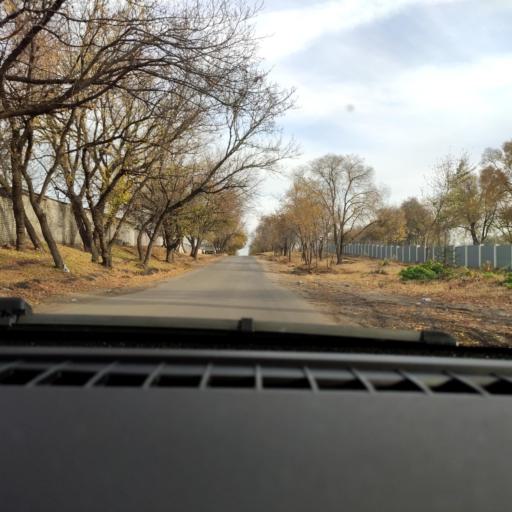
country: RU
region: Voronezj
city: Voronezh
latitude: 51.6598
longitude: 39.2874
